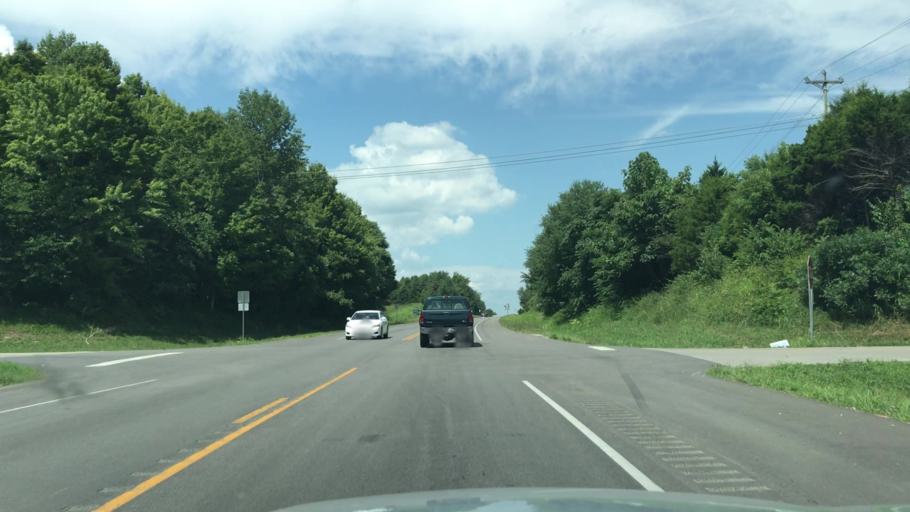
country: US
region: Kentucky
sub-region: Clinton County
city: Albany
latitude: 36.7534
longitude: -85.1178
